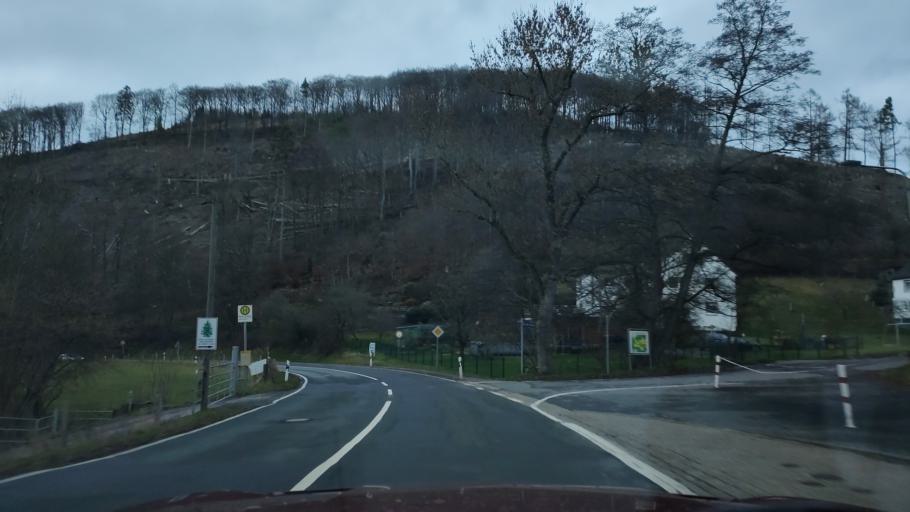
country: DE
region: North Rhine-Westphalia
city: Altena
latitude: 51.3346
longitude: 7.6772
